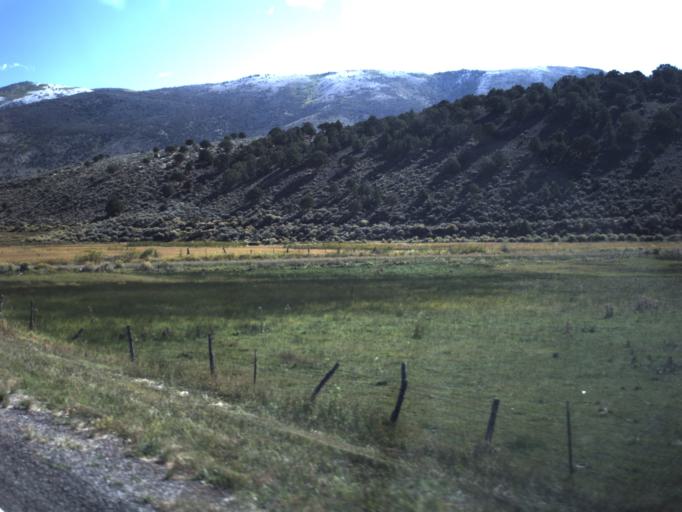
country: US
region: Utah
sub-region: Wayne County
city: Loa
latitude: 38.5627
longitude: -111.8516
